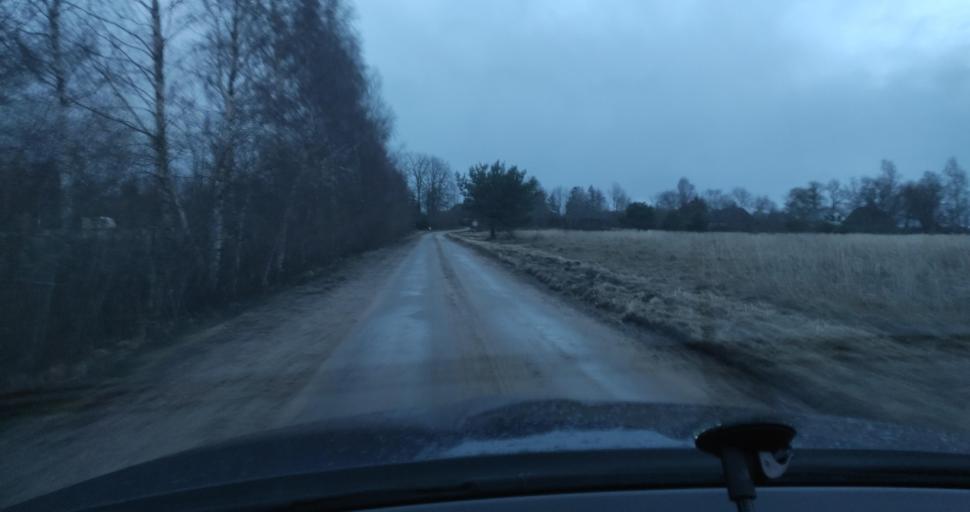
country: LV
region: Pavilostas
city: Pavilosta
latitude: 56.7361
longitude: 21.0713
